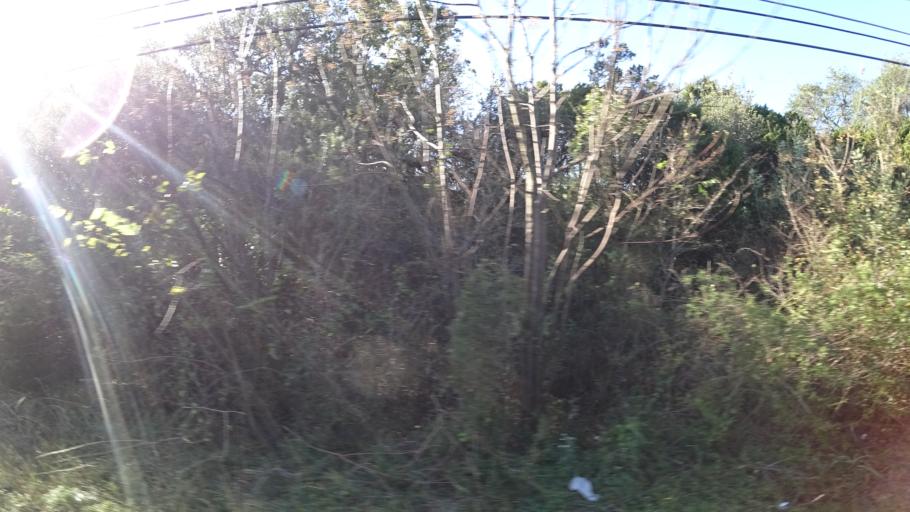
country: US
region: Texas
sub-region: Travis County
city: Barton Creek
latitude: 30.2502
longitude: -97.8484
